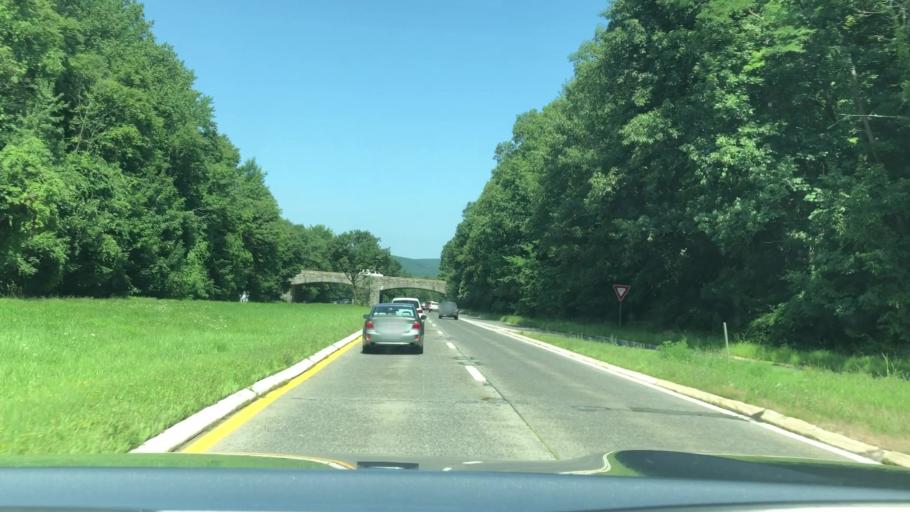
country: US
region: New York
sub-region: Rockland County
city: Pomona
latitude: 41.1707
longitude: -74.0315
